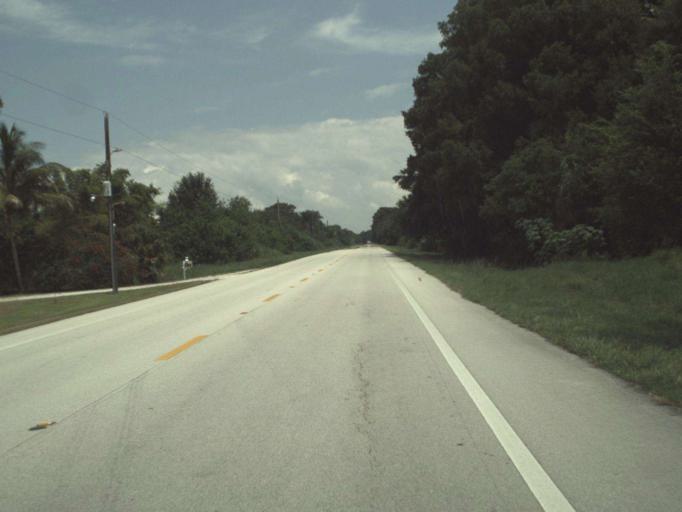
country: US
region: Florida
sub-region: Martin County
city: Indiantown
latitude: 27.0374
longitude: -80.6373
